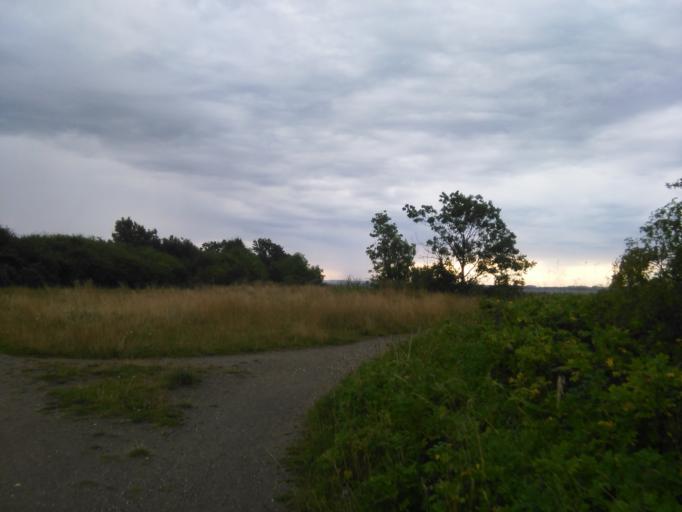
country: DK
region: Central Jutland
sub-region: Arhus Kommune
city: Hjortshoj
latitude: 56.2071
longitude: 10.2846
